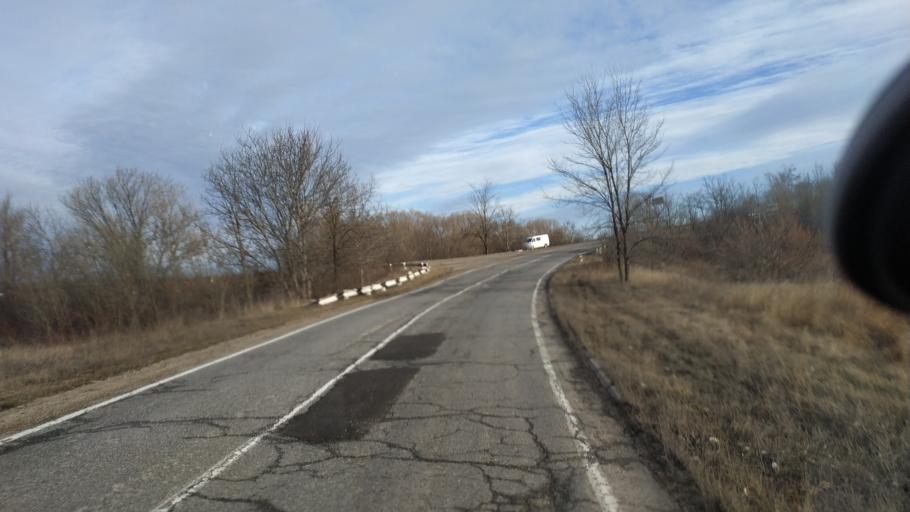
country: MD
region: Chisinau
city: Vadul lui Voda
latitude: 47.0719
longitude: 29.0202
